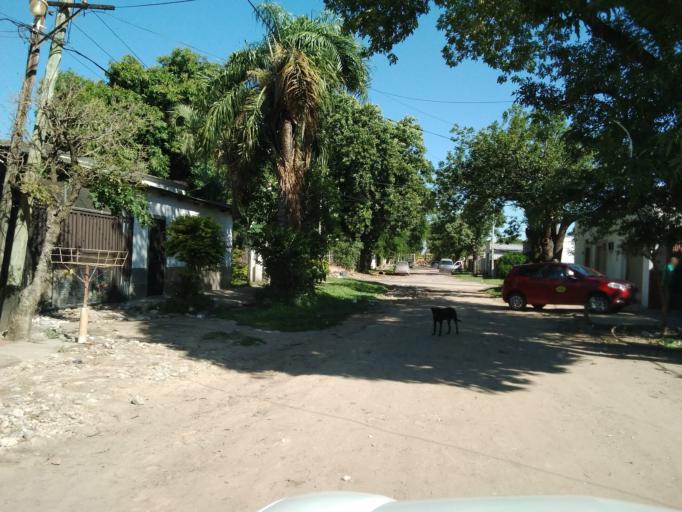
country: AR
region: Corrientes
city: Corrientes
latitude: -27.4815
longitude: -58.8092
